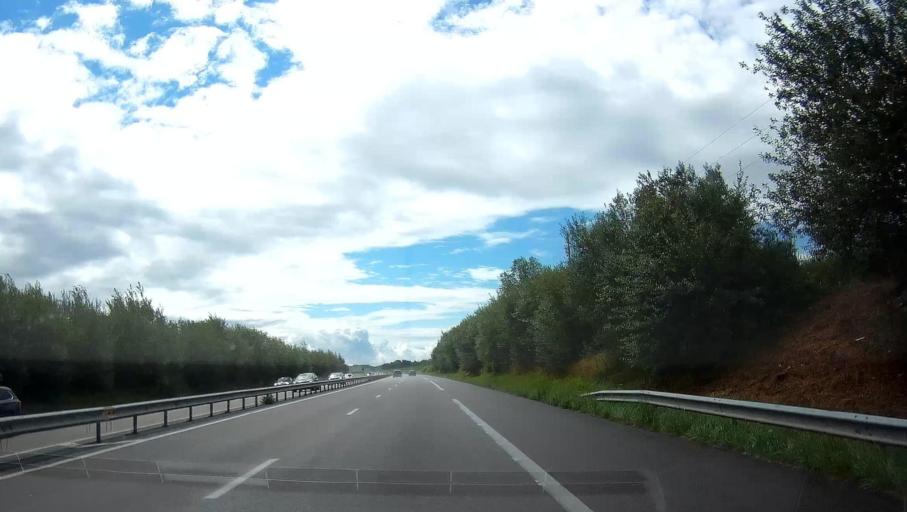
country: FR
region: Champagne-Ardenne
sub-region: Departement de l'Aube
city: Verrieres
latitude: 48.2501
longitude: 4.1678
